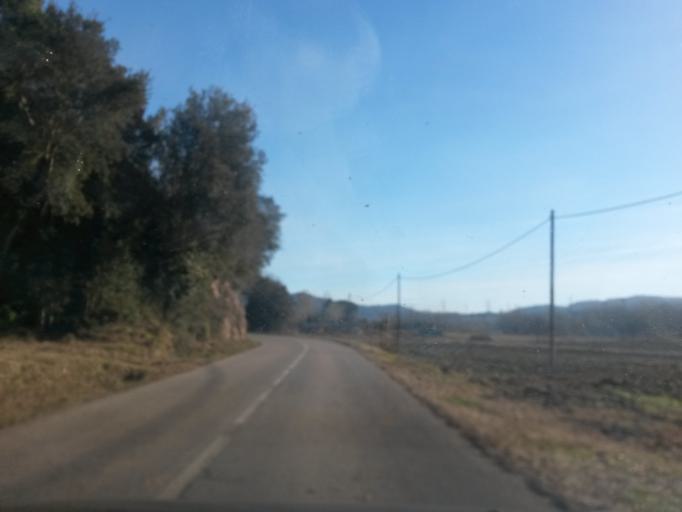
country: ES
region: Catalonia
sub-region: Provincia de Girona
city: Angles
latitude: 41.9784
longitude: 2.6791
